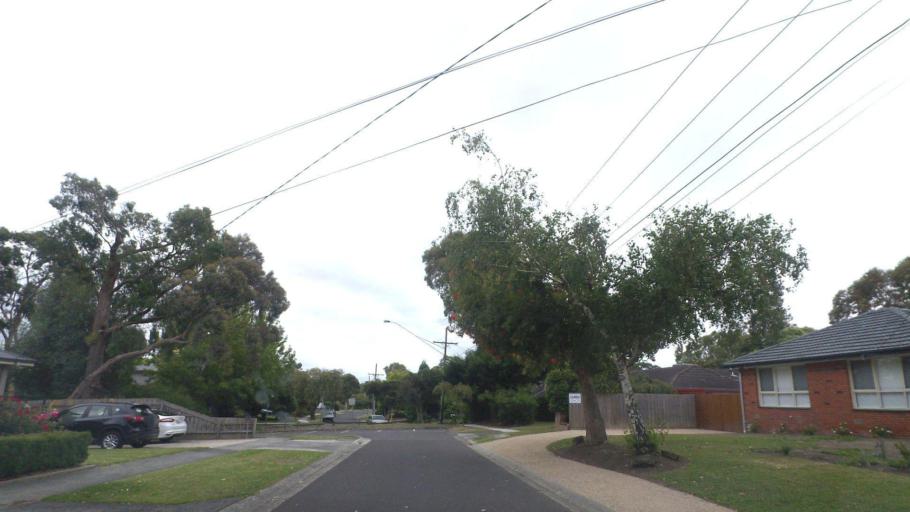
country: AU
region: Victoria
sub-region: Knox
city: The Basin
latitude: -37.8553
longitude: 145.3057
